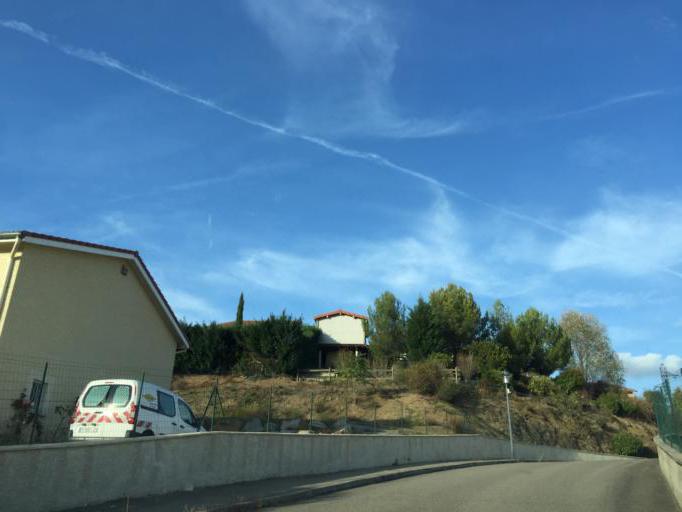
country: FR
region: Rhone-Alpes
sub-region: Departement de la Loire
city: La Grand-Croix
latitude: 45.4965
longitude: 4.5506
